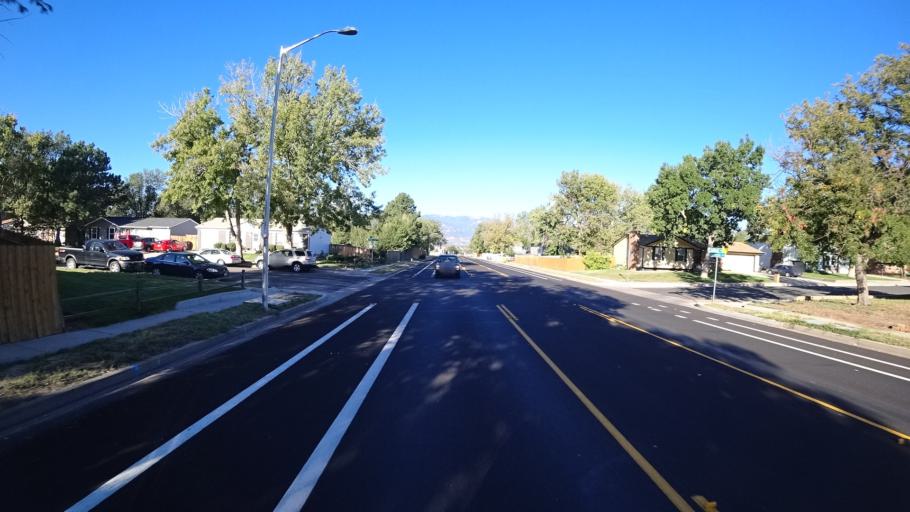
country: US
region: Colorado
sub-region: El Paso County
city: Stratmoor
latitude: 38.7966
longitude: -104.7530
